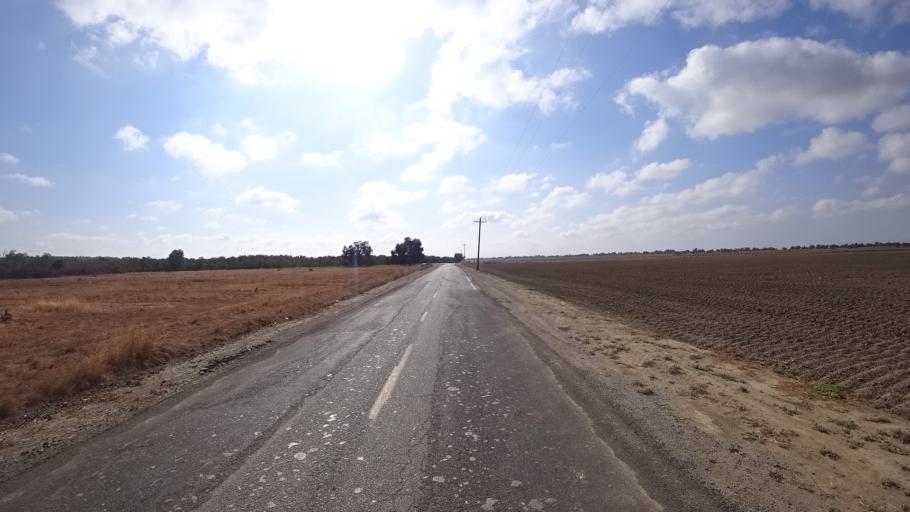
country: US
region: California
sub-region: Yolo County
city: Woodland
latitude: 38.7939
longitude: -121.7004
